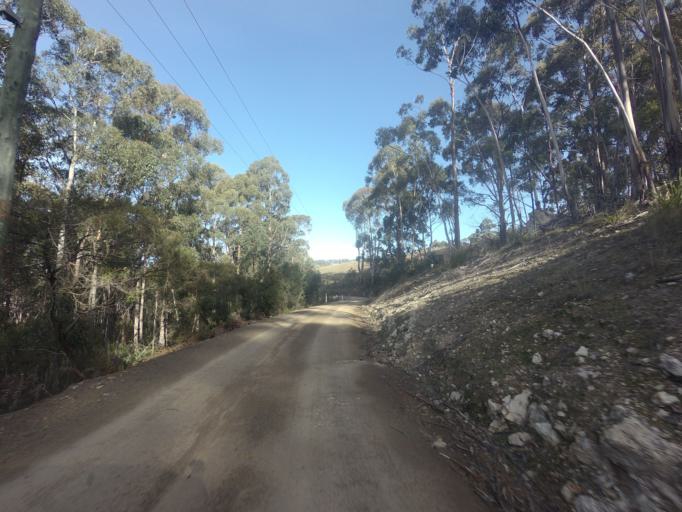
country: AU
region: Tasmania
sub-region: Kingborough
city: Kettering
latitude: -43.1029
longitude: 147.2600
